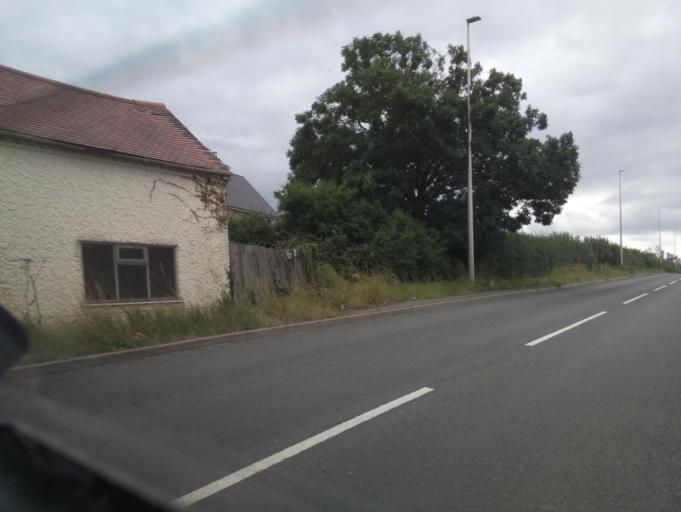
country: GB
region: England
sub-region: Nottinghamshire
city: Bingham
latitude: 52.9635
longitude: -0.9625
